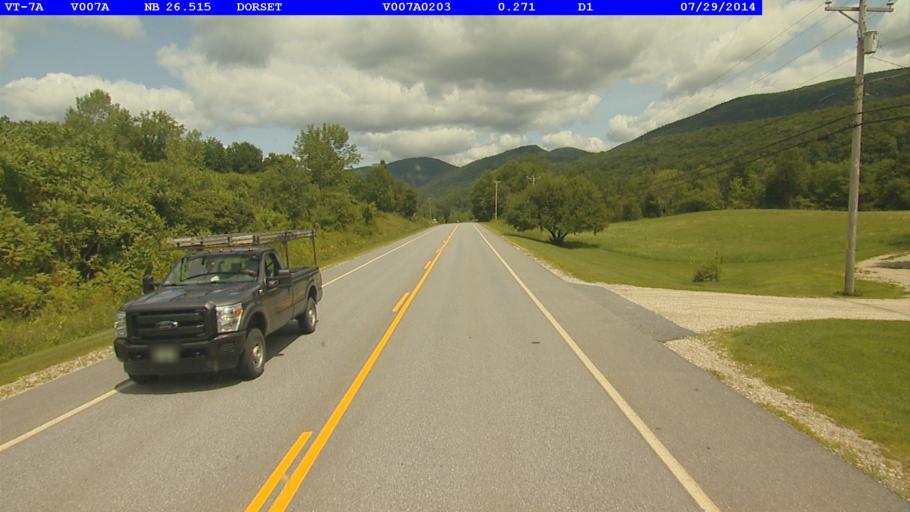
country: US
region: Vermont
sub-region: Bennington County
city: Manchester Center
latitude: 43.2144
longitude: -73.0167
